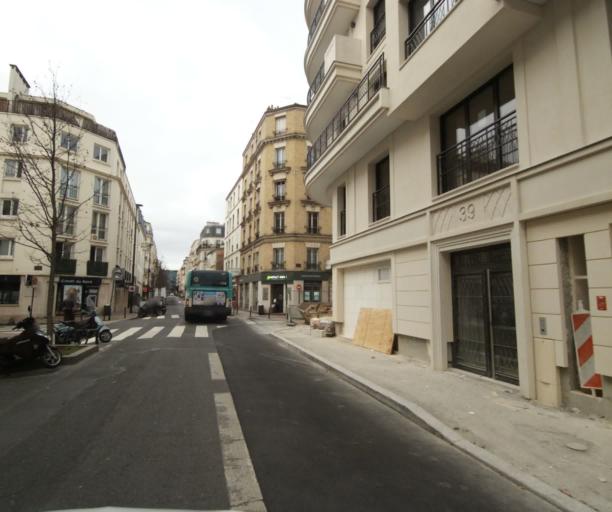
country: FR
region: Ile-de-France
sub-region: Departement des Hauts-de-Seine
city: Levallois-Perret
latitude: 48.8908
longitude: 2.2846
